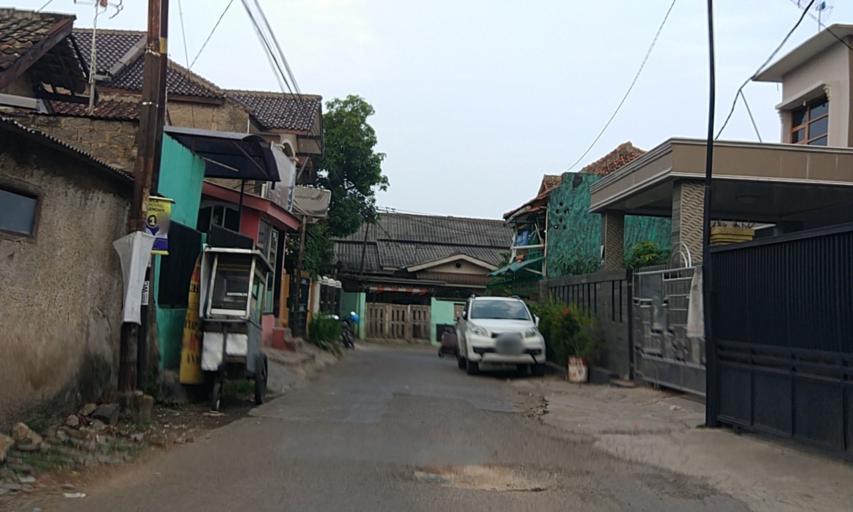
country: ID
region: West Java
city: Bandung
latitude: -6.9091
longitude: 107.6785
